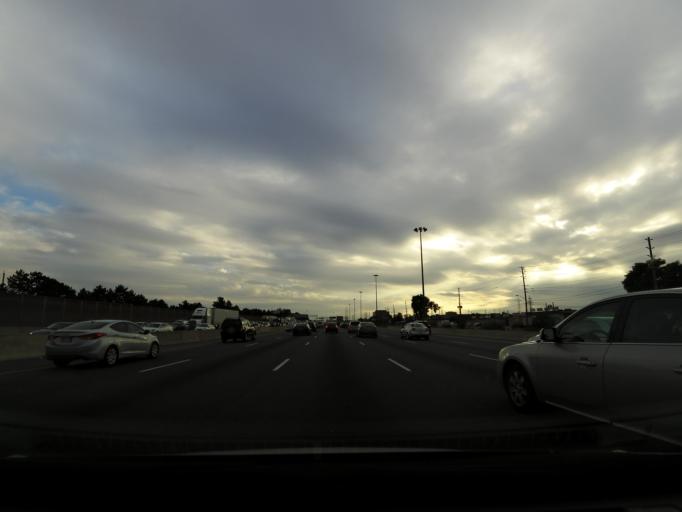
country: CA
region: Ontario
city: Etobicoke
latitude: 43.7004
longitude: -79.5621
